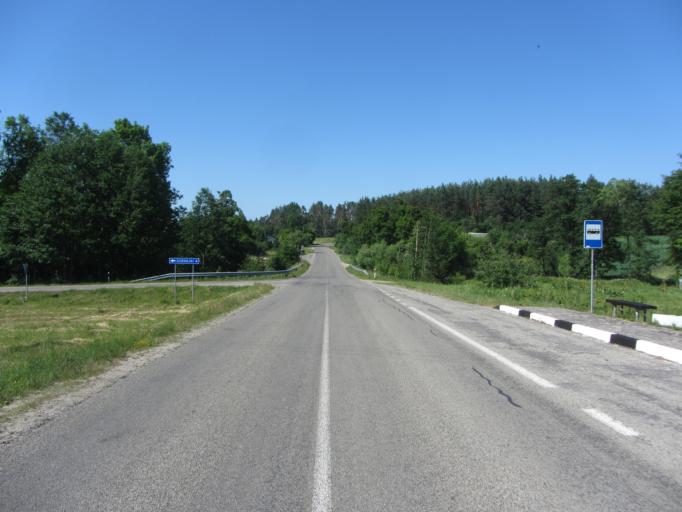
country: LT
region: Alytaus apskritis
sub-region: Alytus
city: Alytus
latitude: 54.3456
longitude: 24.1063
